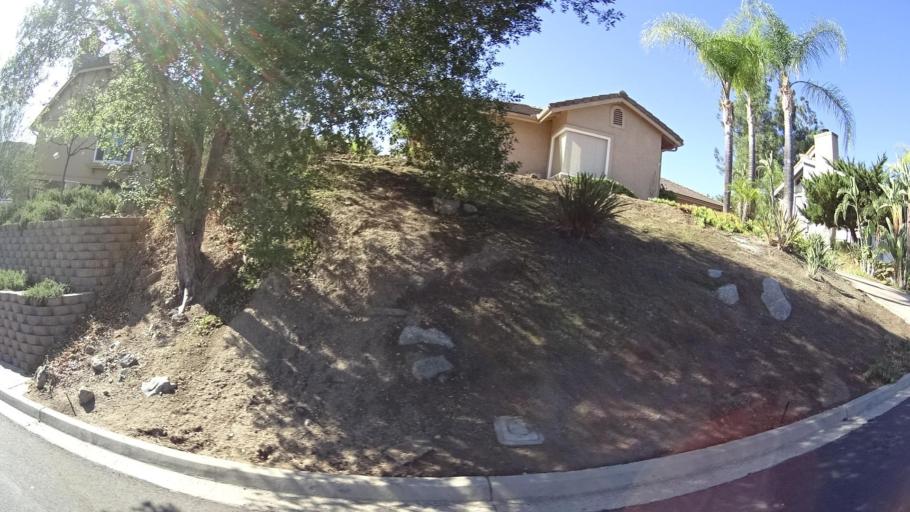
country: US
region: California
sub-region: San Diego County
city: San Diego Country Estates
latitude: 32.9991
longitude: -116.8136
